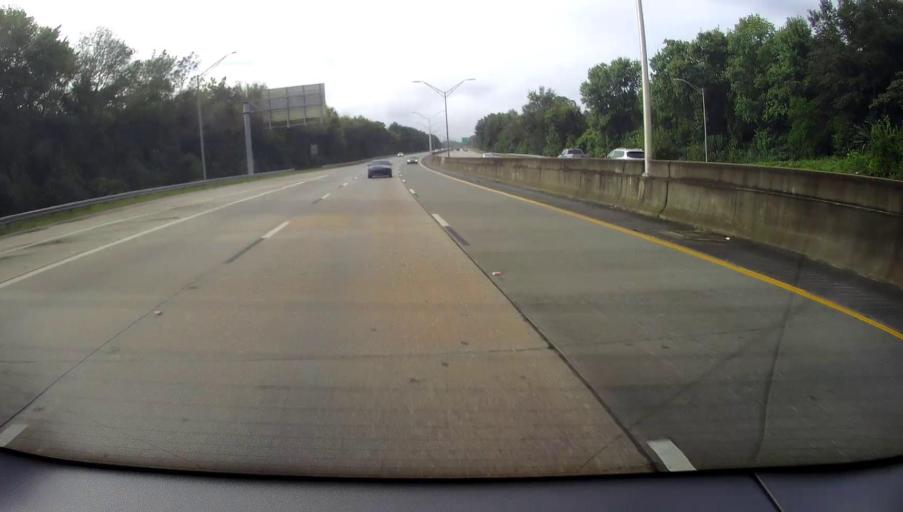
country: US
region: Georgia
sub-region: Bibb County
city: Macon
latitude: 32.8105
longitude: -83.6560
